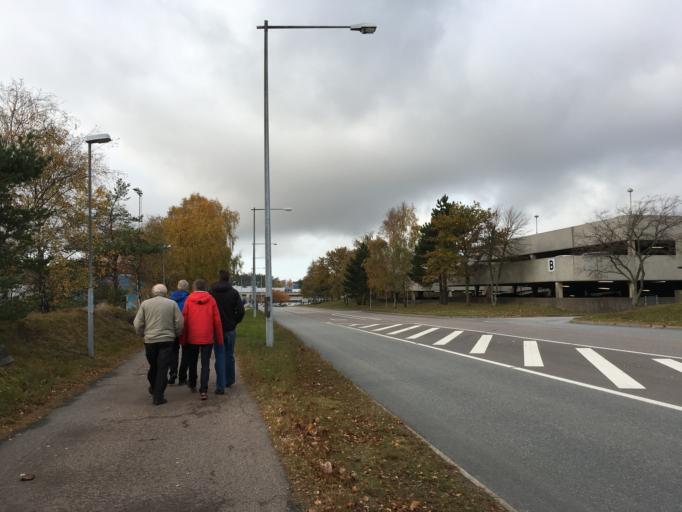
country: SE
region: Vaestra Goetaland
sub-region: Goteborg
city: Majorna
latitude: 57.7266
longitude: 11.8639
